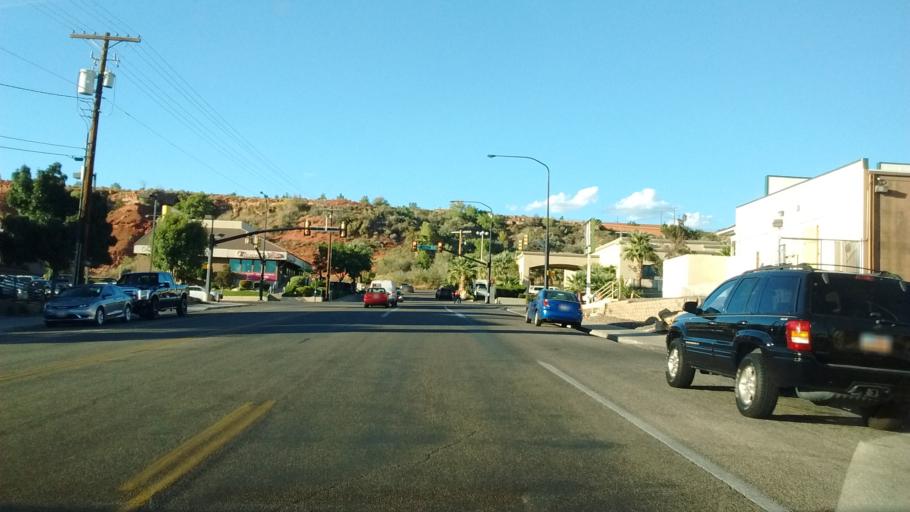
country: US
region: Utah
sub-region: Washington County
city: Saint George
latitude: 37.1091
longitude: -113.5684
